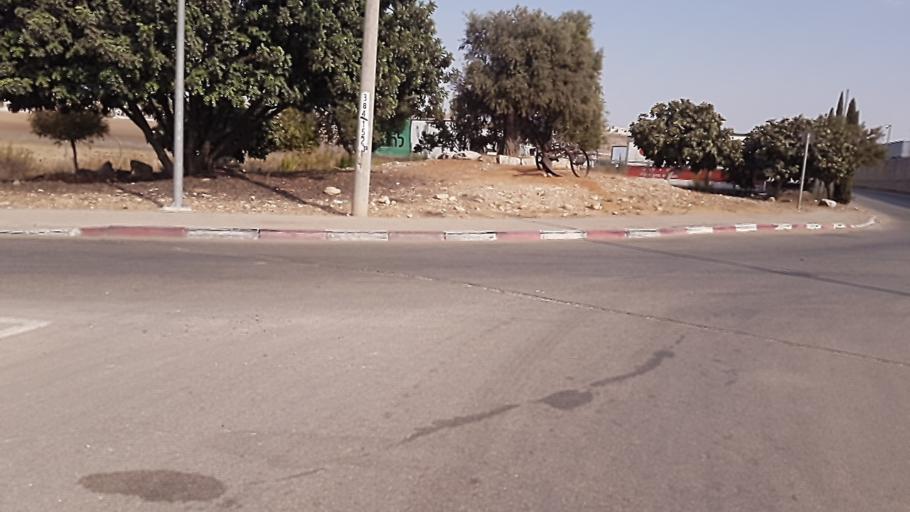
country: IL
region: Central District
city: Rosh Ha'Ayin
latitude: 32.0851
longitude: 34.9416
